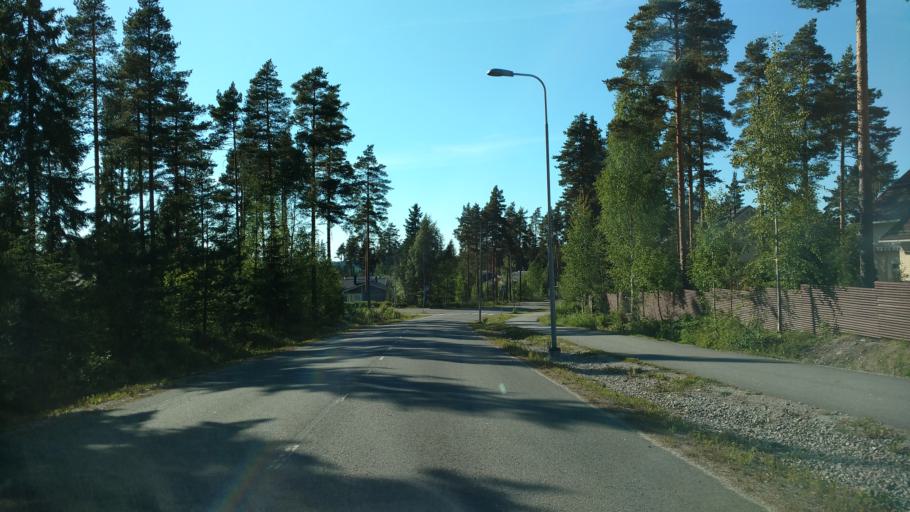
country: FI
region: Varsinais-Suomi
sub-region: Salo
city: Salo
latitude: 60.4017
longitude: 23.1897
